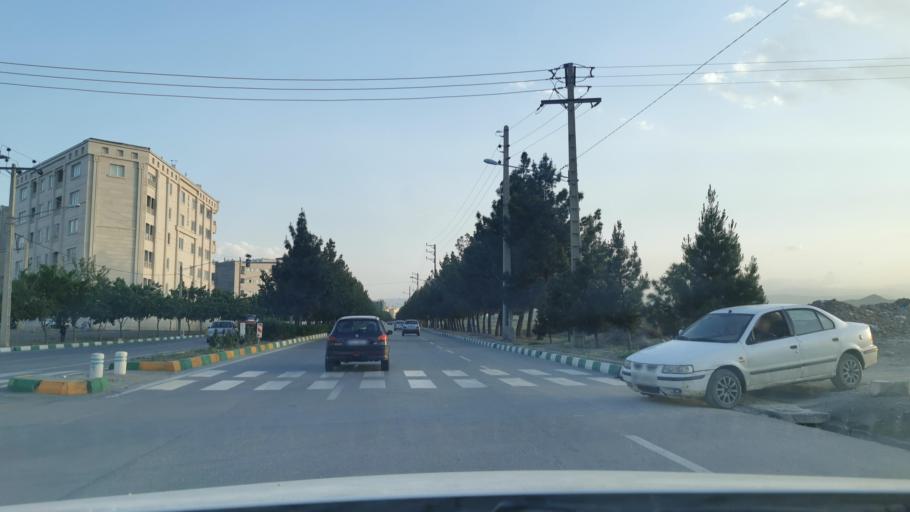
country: IR
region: Razavi Khorasan
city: Torqabeh
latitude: 36.3863
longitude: 59.4656
